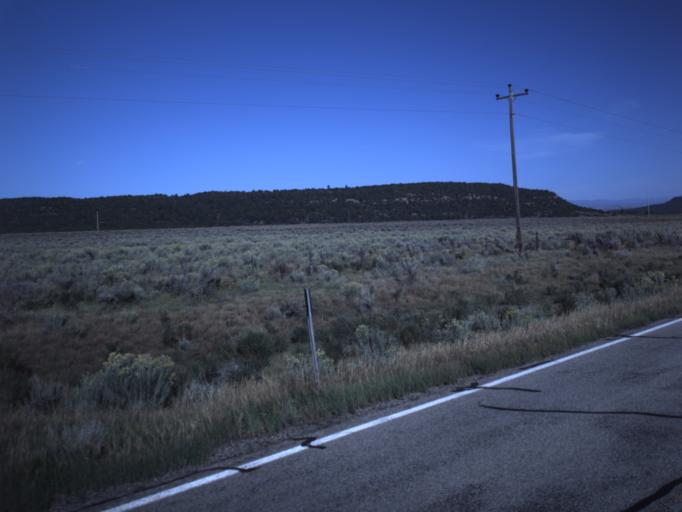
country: US
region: Utah
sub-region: Grand County
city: Moab
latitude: 38.3335
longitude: -109.1544
